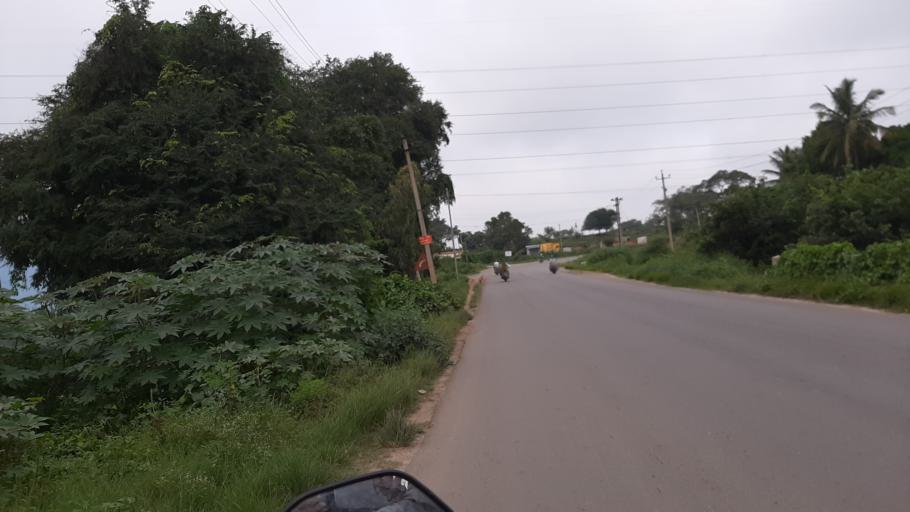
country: IN
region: Karnataka
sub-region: Bangalore Rural
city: Nelamangala
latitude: 12.9653
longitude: 77.3926
